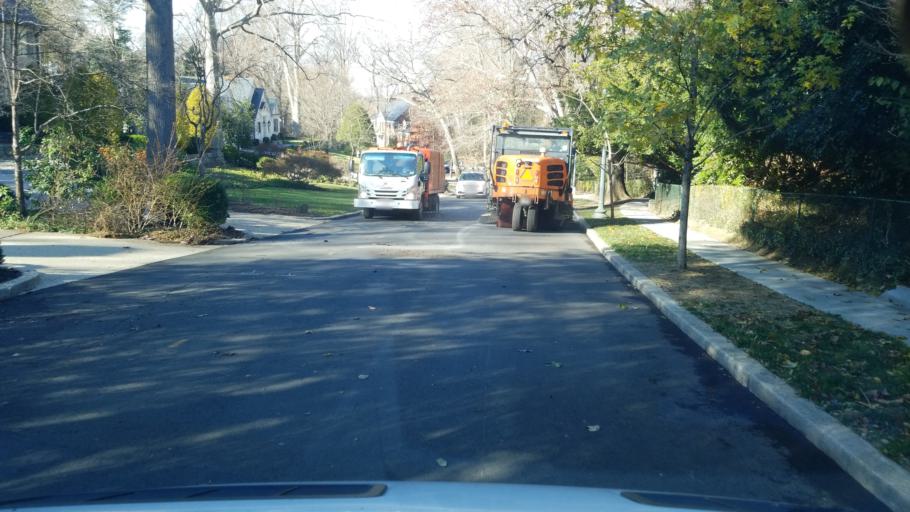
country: US
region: Maryland
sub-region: Montgomery County
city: Brookmont
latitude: 38.9352
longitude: -77.0982
